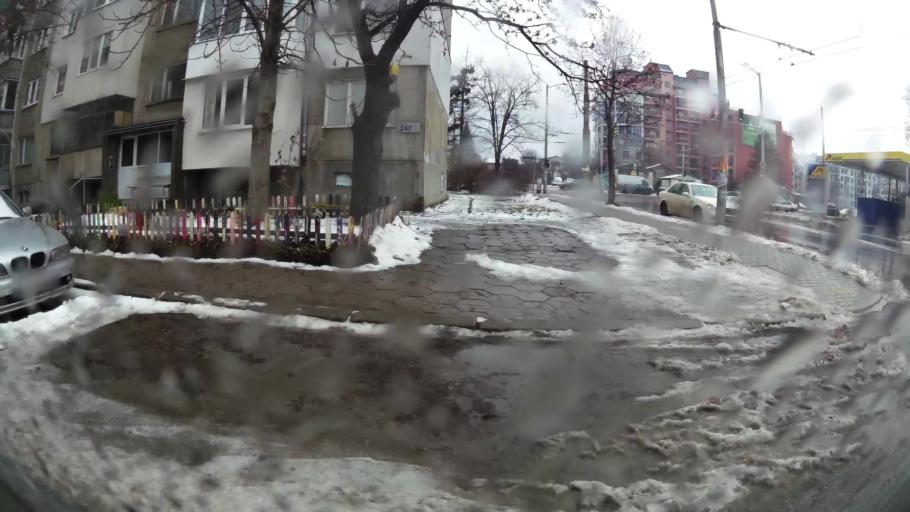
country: BG
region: Sofia-Capital
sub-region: Stolichna Obshtina
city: Sofia
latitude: 42.6620
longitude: 23.2957
